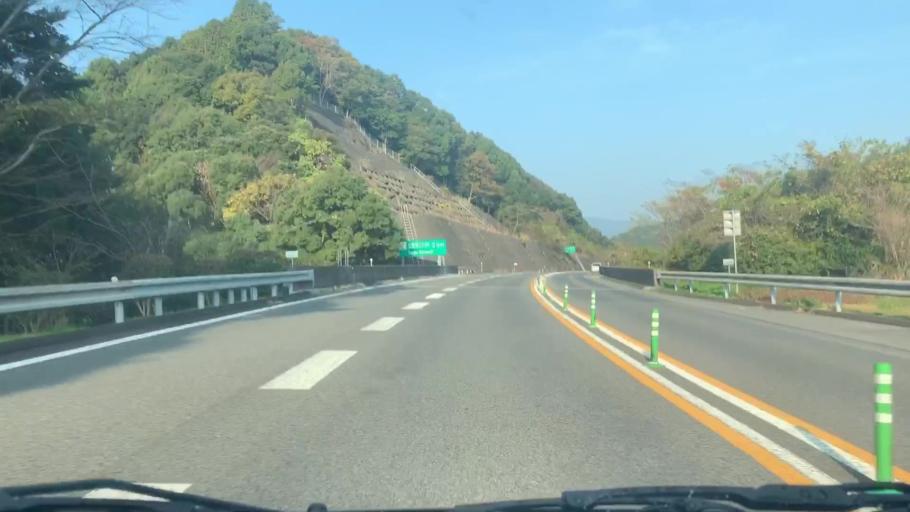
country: JP
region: Saga Prefecture
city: Imaricho-ko
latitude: 33.1603
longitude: 129.8663
